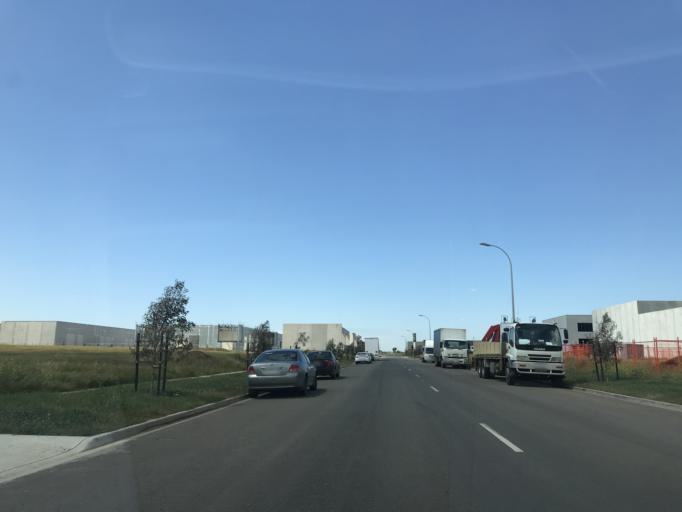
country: AU
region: Victoria
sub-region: Wyndham
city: Truganina
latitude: -37.8369
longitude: 144.7417
